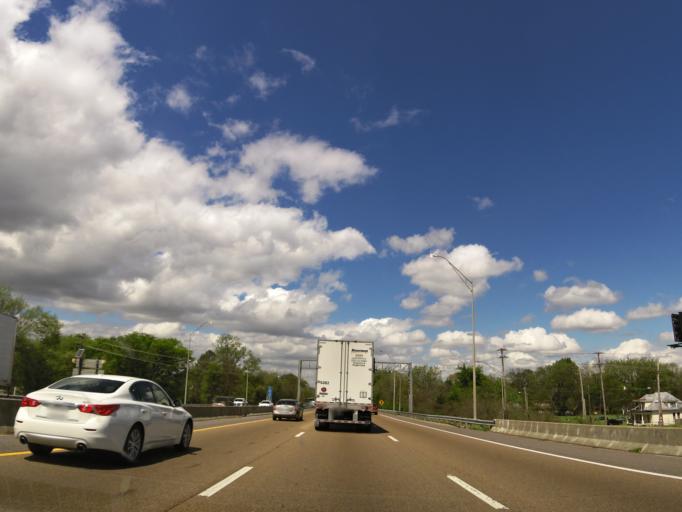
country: US
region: Tennessee
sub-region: Shelby County
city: Memphis
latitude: 35.1743
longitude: -90.0183
